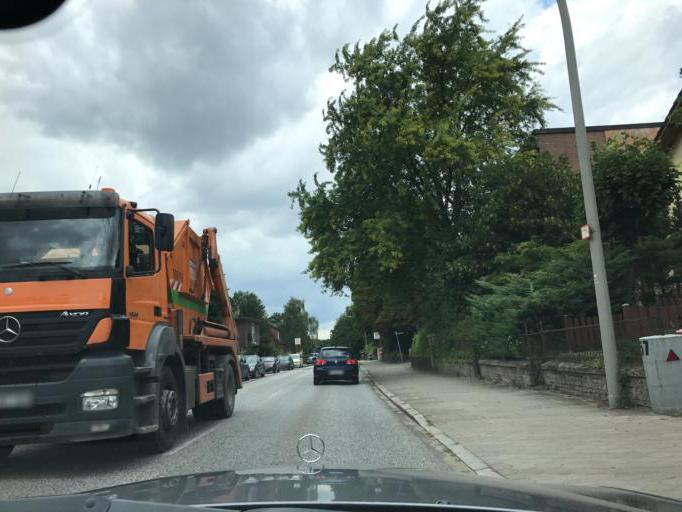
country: DE
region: Hamburg
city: Wandsbek
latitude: 53.5311
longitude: 10.1234
